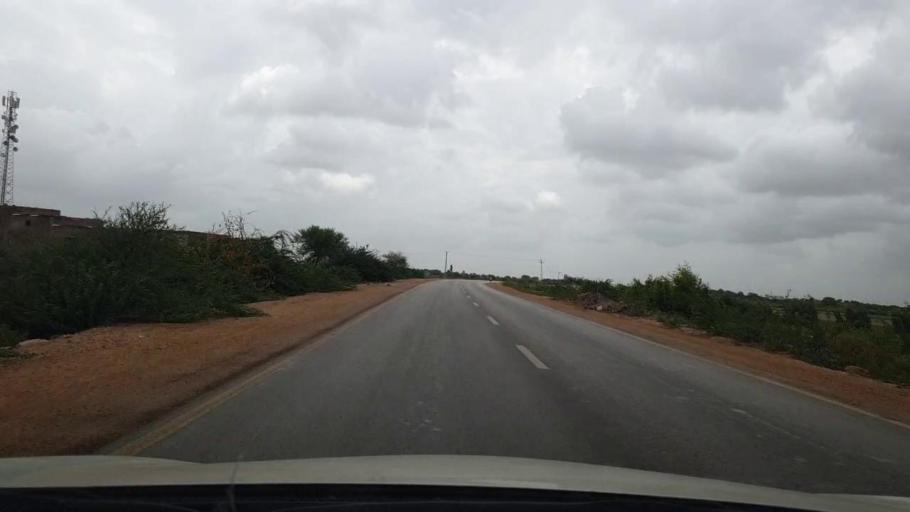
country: PK
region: Sindh
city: Mirpur Batoro
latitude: 24.6428
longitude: 68.4019
